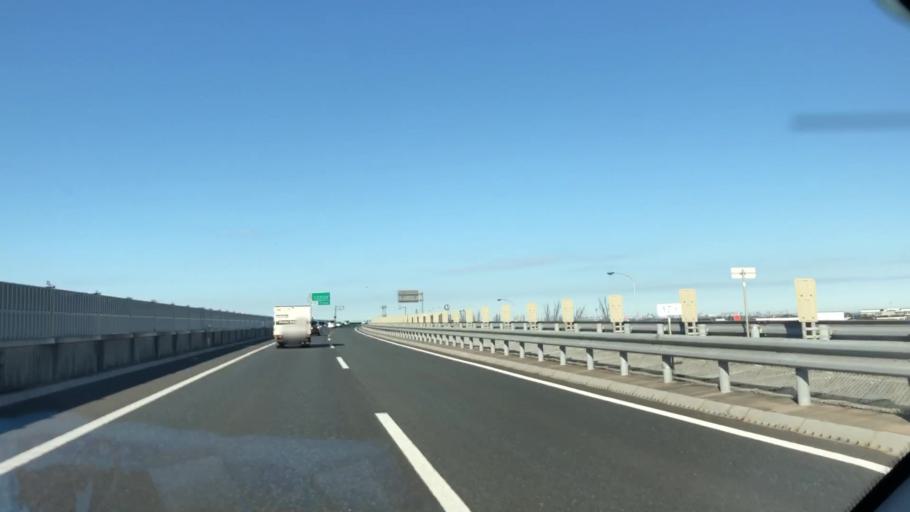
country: JP
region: Chiba
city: Kisarazu
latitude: 35.4213
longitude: 139.9372
